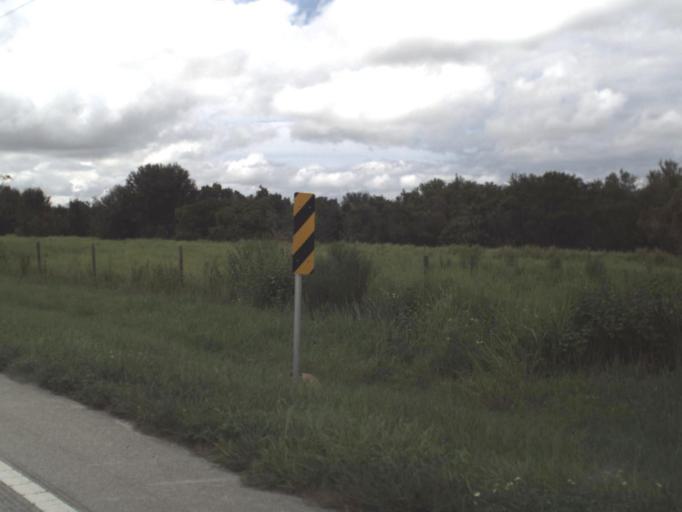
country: US
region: Florida
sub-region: Hardee County
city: Bowling Green
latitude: 27.5949
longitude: -81.9869
